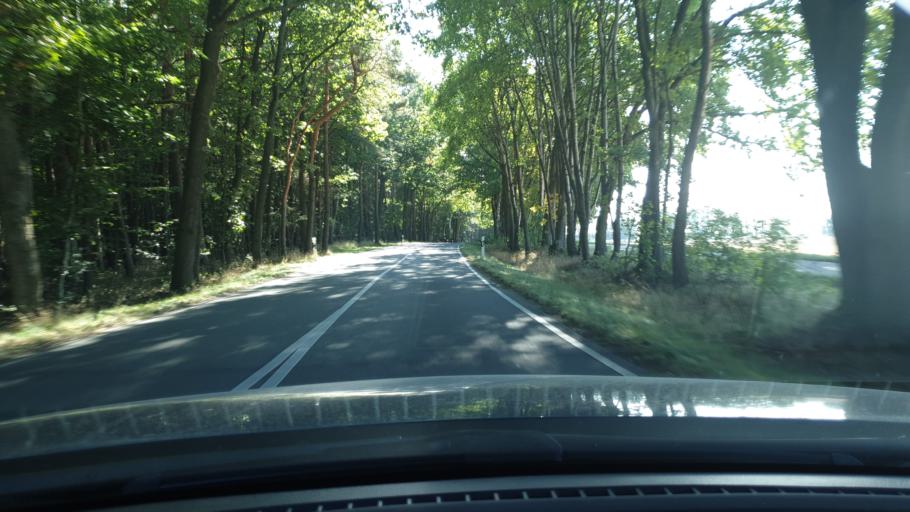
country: DE
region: Mecklenburg-Vorpommern
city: Wittenburg
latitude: 53.4963
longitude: 11.0085
